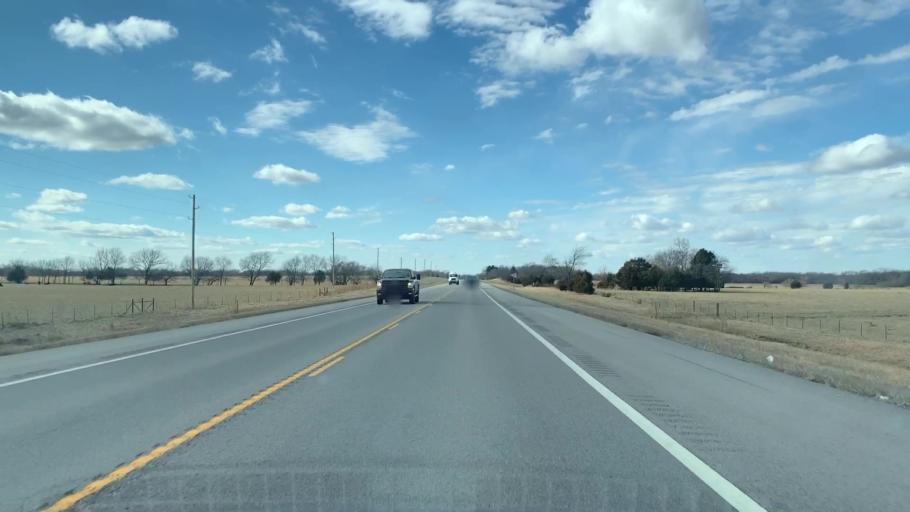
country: US
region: Kansas
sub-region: Labette County
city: Oswego
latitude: 37.3401
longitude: -95.0509
